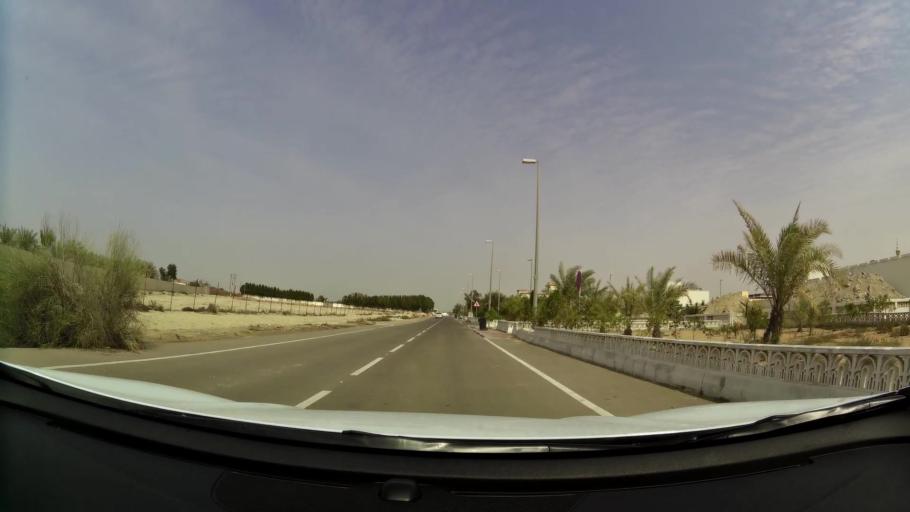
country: AE
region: Abu Dhabi
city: Abu Dhabi
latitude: 24.5462
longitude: 54.6617
